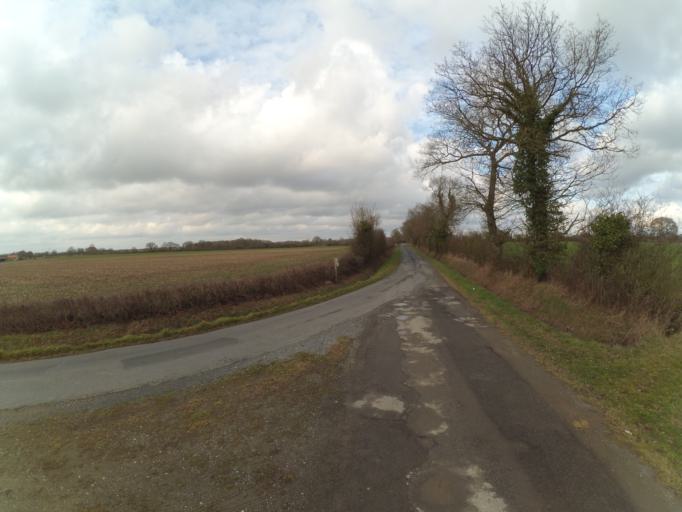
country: FR
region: Pays de la Loire
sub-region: Departement de la Loire-Atlantique
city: Saint-Hilaire-de-Clisson
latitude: 47.0604
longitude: -1.2868
